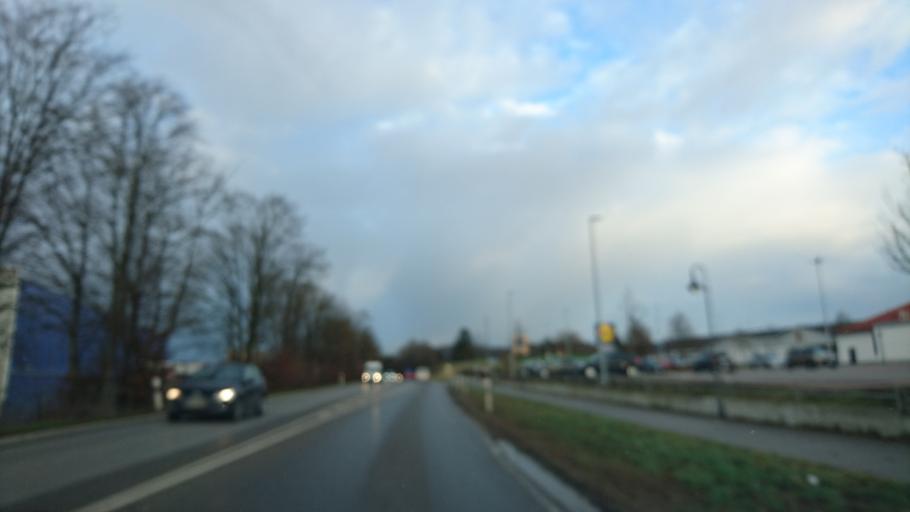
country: DE
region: Bavaria
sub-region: Swabia
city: Diedorf
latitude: 48.3600
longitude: 10.7853
